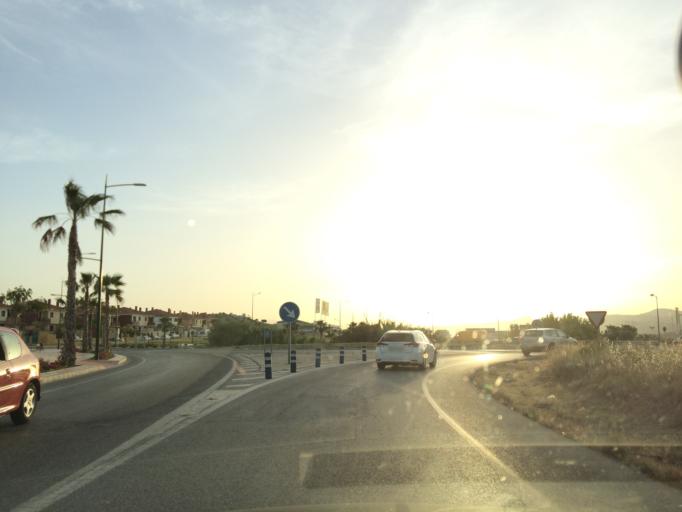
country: ES
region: Andalusia
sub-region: Provincia de Malaga
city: Alhaurin de la Torre
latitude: 36.6682
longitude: -4.5450
